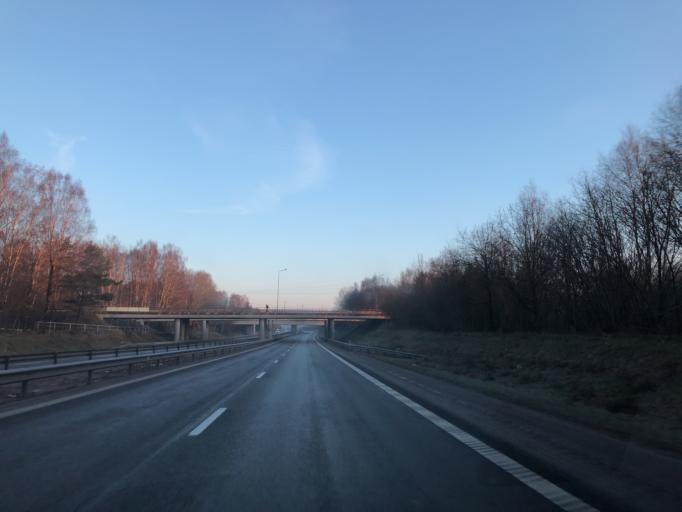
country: SE
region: Halland
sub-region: Halmstads Kommun
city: Halmstad
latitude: 56.6854
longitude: 12.8952
